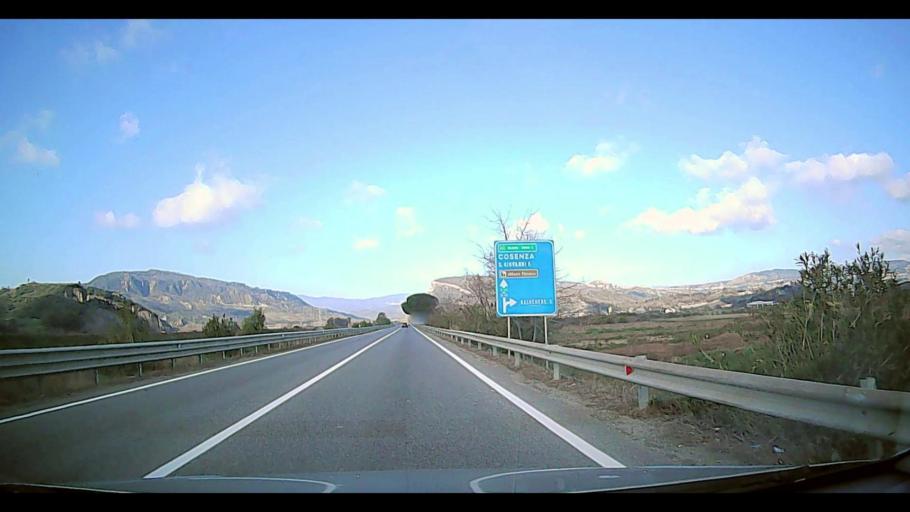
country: IT
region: Calabria
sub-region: Provincia di Crotone
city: Santa Severina
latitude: 39.1780
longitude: 16.9255
